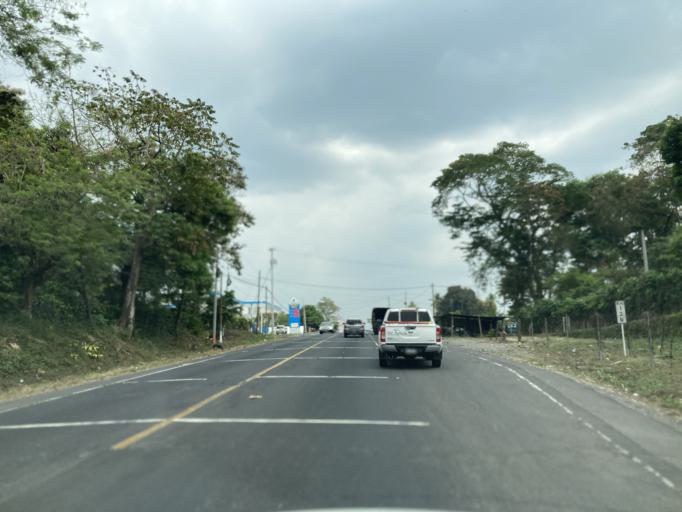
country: GT
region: Suchitepeque
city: Rio Bravo
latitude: 14.4117
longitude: -91.3089
